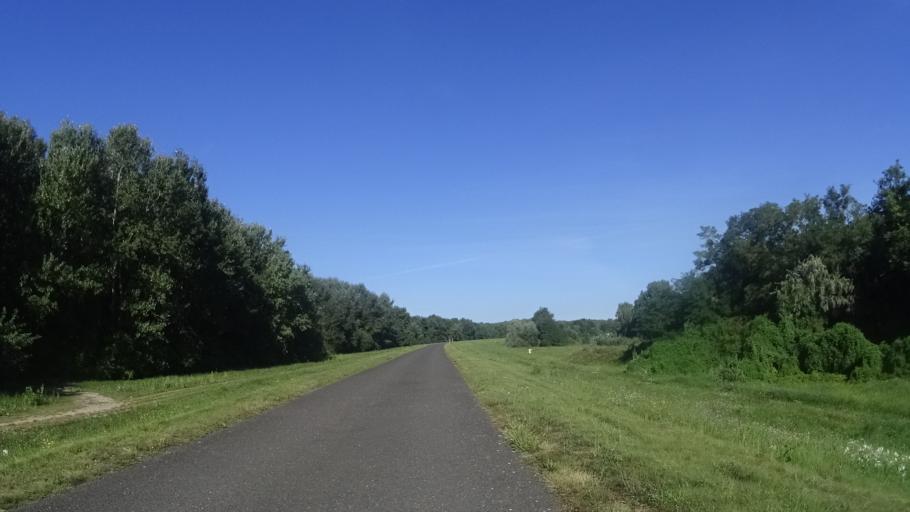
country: HU
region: Gyor-Moson-Sopron
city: Rajka
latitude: 48.0631
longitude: 17.1829
